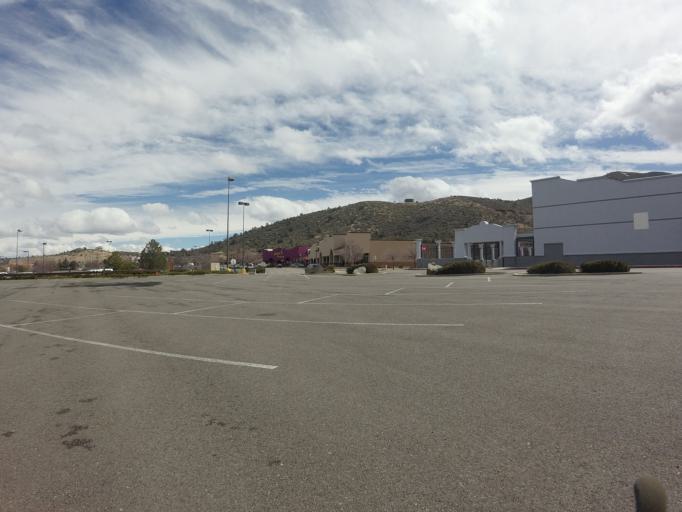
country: US
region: Arizona
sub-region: Yavapai County
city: Prescott
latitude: 34.5491
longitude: -112.4355
